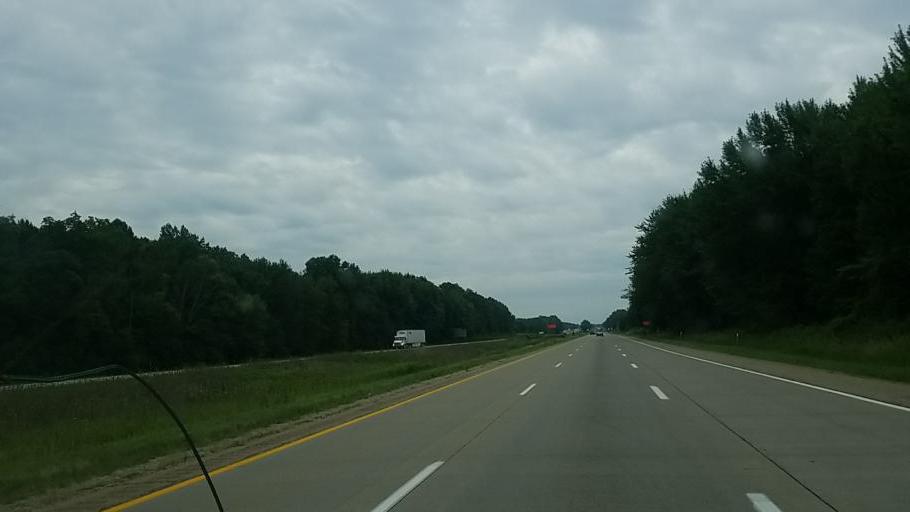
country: US
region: Michigan
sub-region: Branch County
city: Coldwater
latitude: 41.8932
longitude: -84.9911
